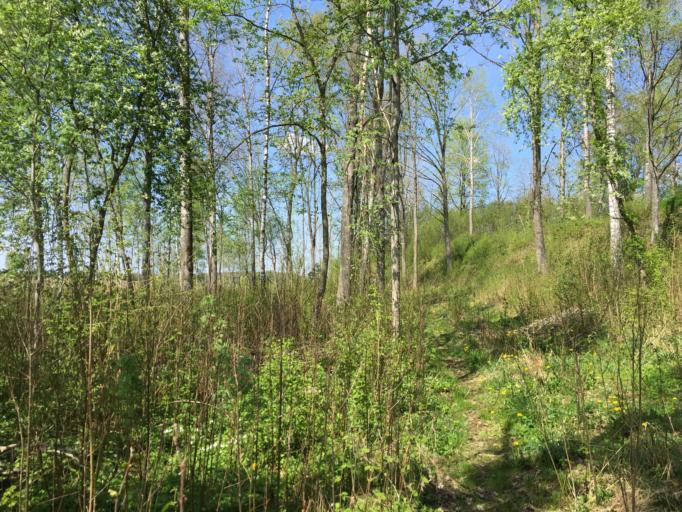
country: LV
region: Limbazu Rajons
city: Limbazi
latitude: 57.3539
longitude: 24.6565
